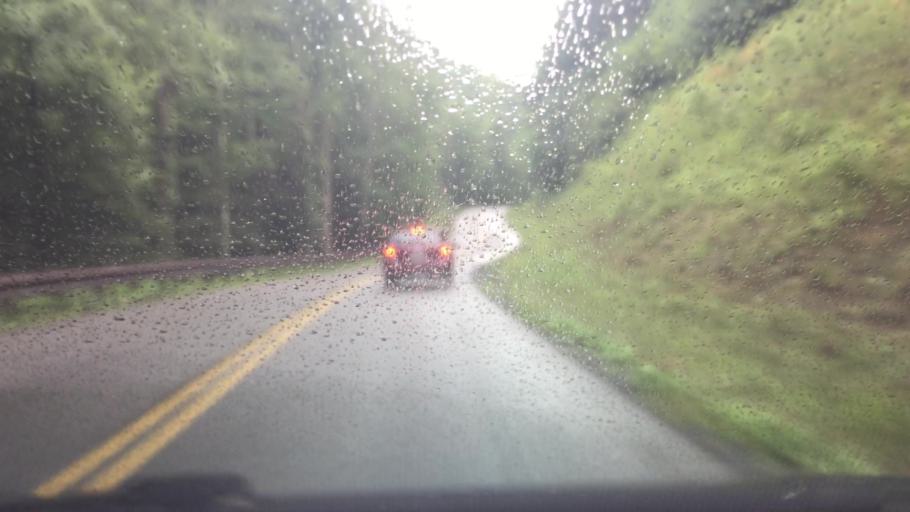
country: US
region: Virginia
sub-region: Smyth County
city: Atkins
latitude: 36.8343
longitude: -81.4167
